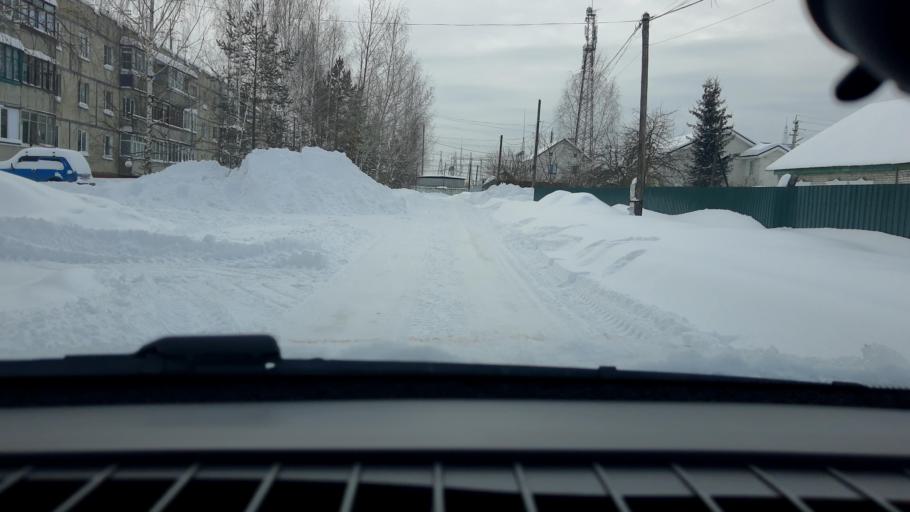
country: RU
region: Nizjnij Novgorod
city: Lukino
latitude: 56.3972
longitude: 43.7026
